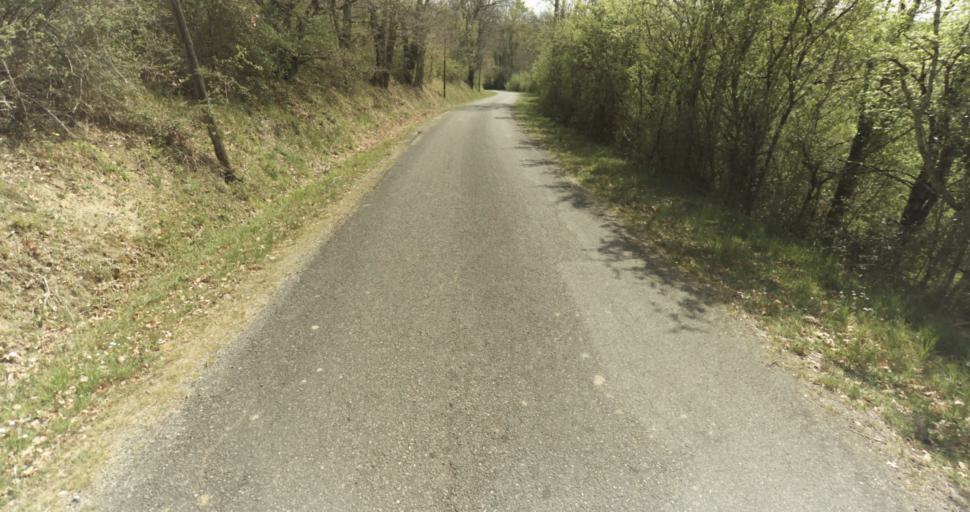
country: FR
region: Midi-Pyrenees
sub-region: Departement du Tarn-et-Garonne
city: Moissac
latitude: 44.1626
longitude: 1.1199
